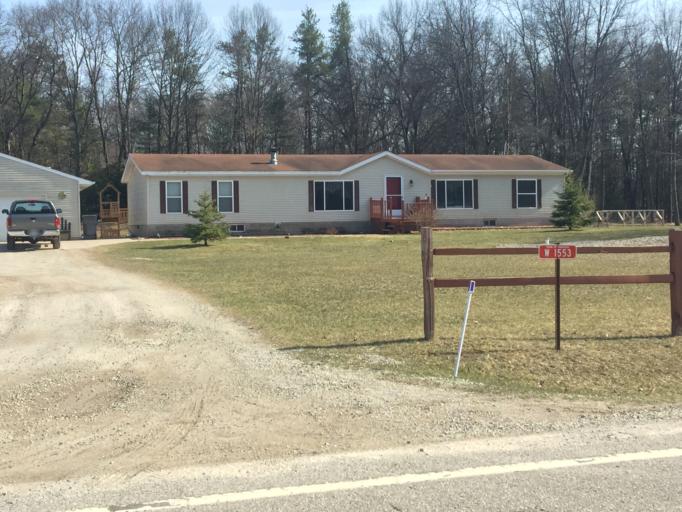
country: US
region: Wisconsin
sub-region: Marinette County
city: Marinette
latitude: 45.0450
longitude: -87.6704
